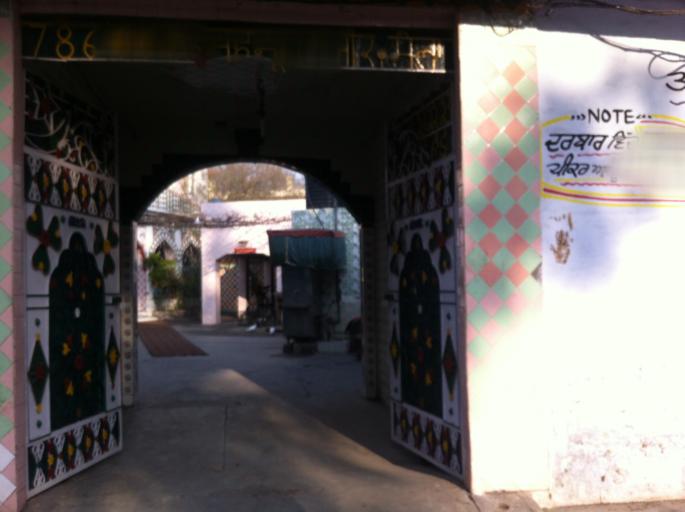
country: IN
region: Punjab
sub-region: Kapurthala
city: Phagwara
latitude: 31.2195
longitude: 75.7729
